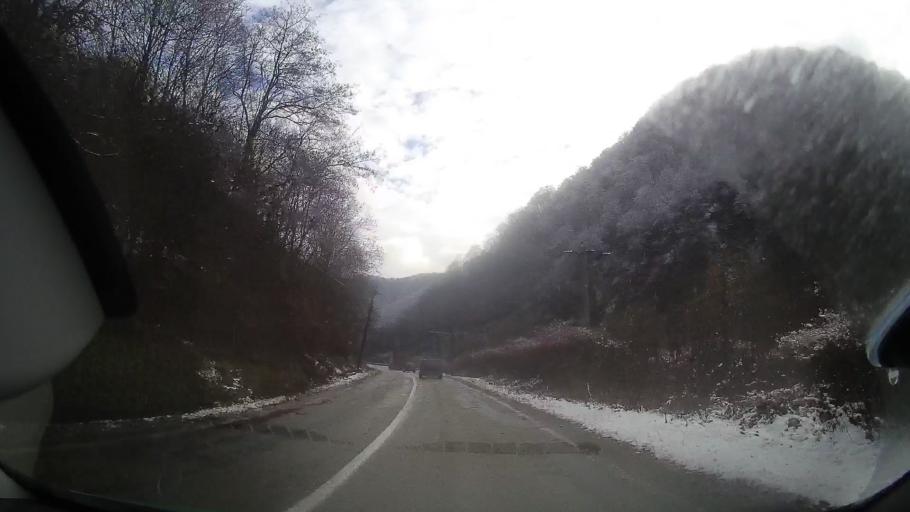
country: RO
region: Alba
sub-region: Oras Baia de Aries
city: Baia de Aries
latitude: 46.4049
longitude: 23.3375
